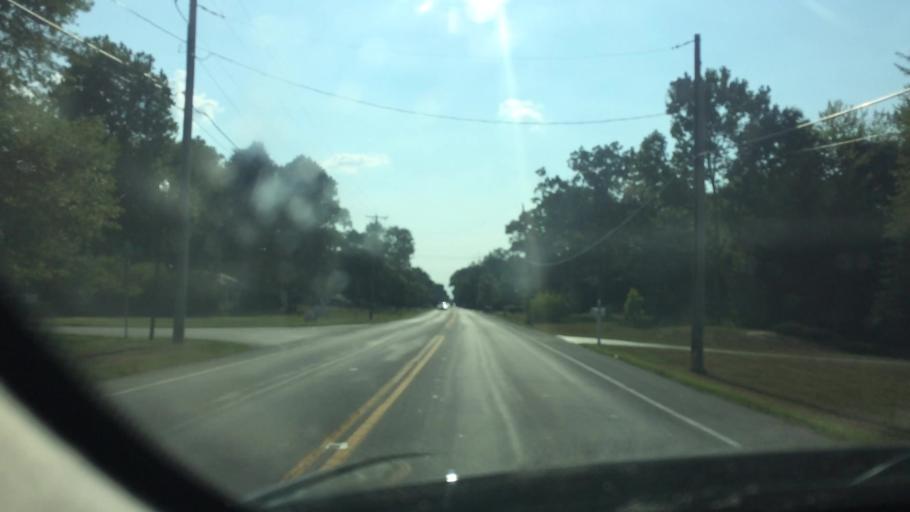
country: US
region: Ohio
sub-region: Lucas County
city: Holland
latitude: 41.6540
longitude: -83.7110
